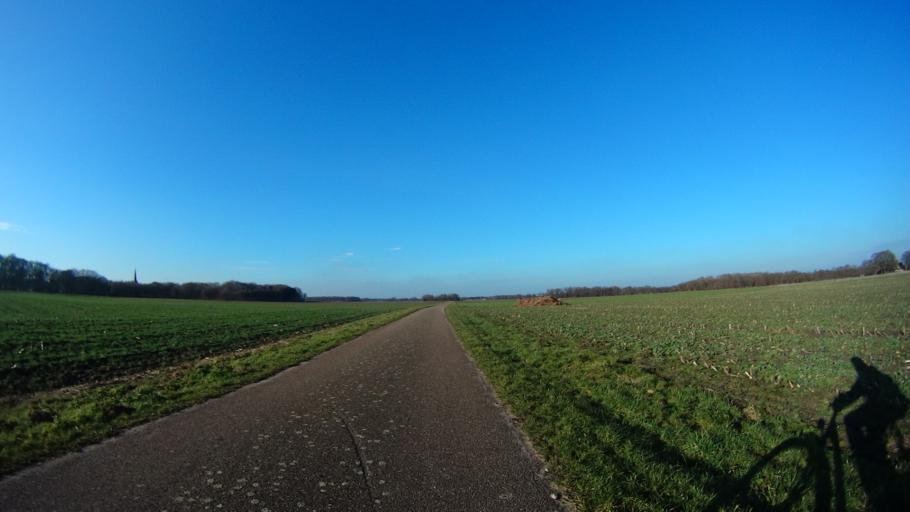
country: NL
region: Drenthe
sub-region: Gemeente Coevorden
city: Sleen
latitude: 52.7737
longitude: 6.8128
